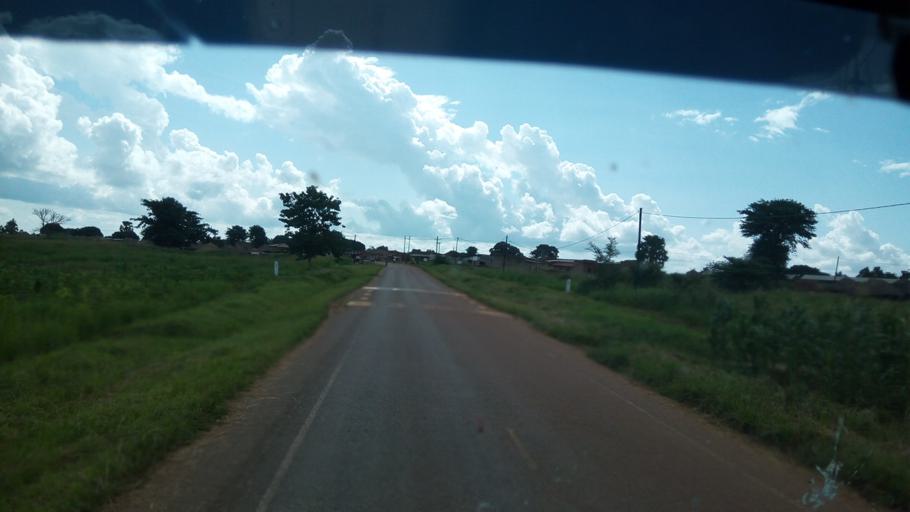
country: UG
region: Northern Region
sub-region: Nwoya District
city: Nwoya
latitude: 2.5337
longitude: 31.8883
